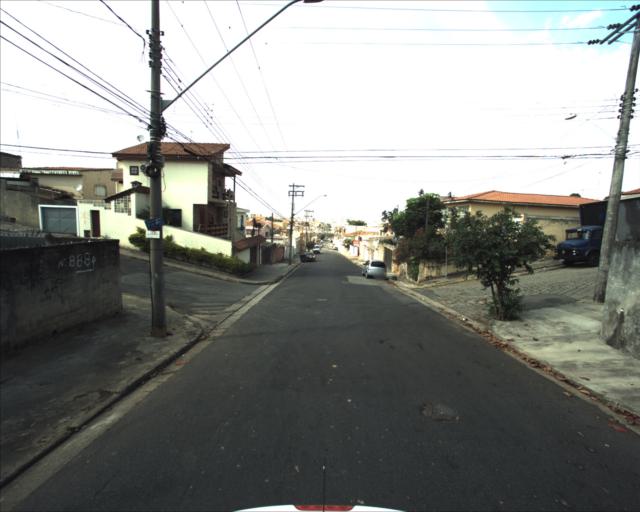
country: BR
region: Sao Paulo
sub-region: Sorocaba
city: Sorocaba
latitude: -23.4866
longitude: -47.4674
